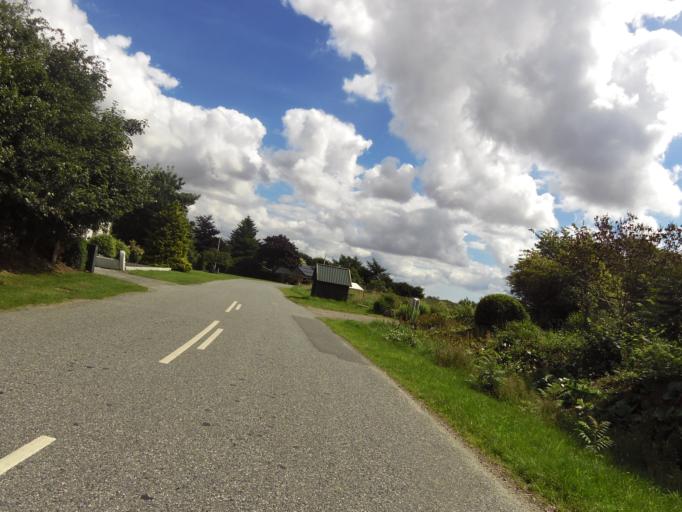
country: DK
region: South Denmark
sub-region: Haderslev Kommune
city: Vojens
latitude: 55.2813
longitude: 9.2061
